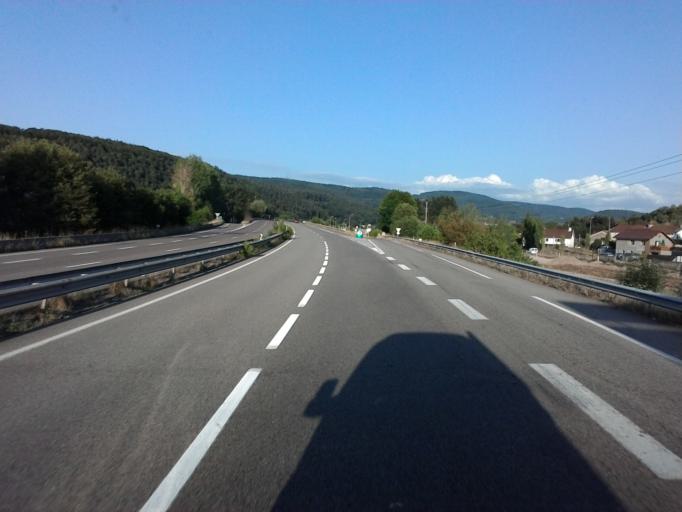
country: FR
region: Lorraine
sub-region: Departement des Vosges
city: Pouxeux
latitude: 48.1103
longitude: 6.5688
